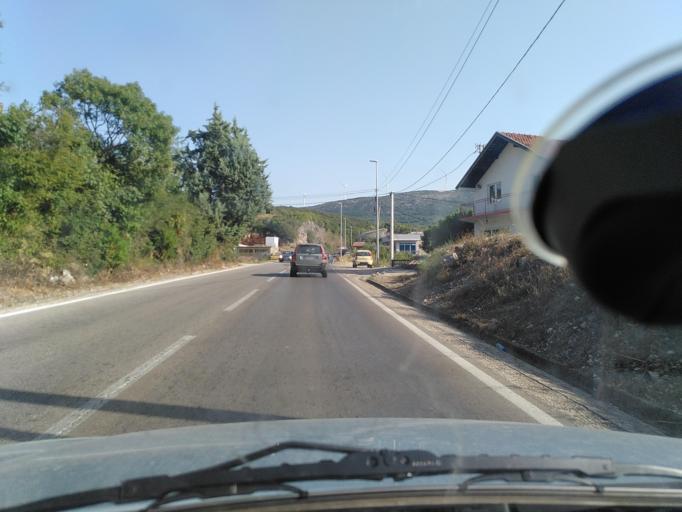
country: ME
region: Ulcinj
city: Ulcinj
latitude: 41.9558
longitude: 19.1910
